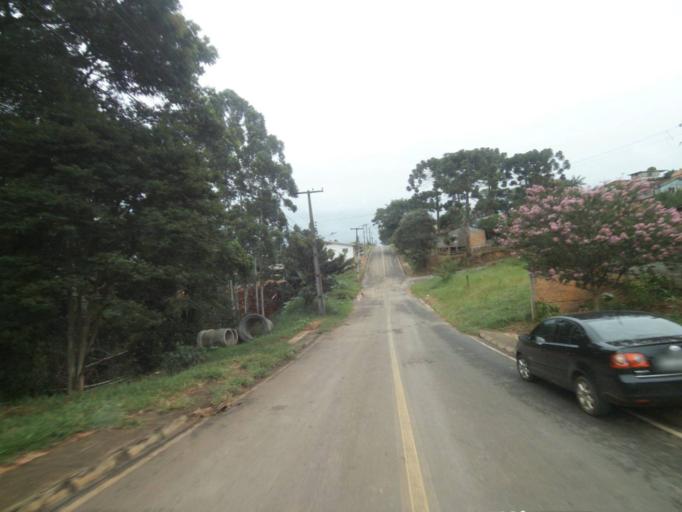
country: BR
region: Parana
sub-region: Telemaco Borba
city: Telemaco Borba
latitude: -24.3203
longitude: -50.6541
